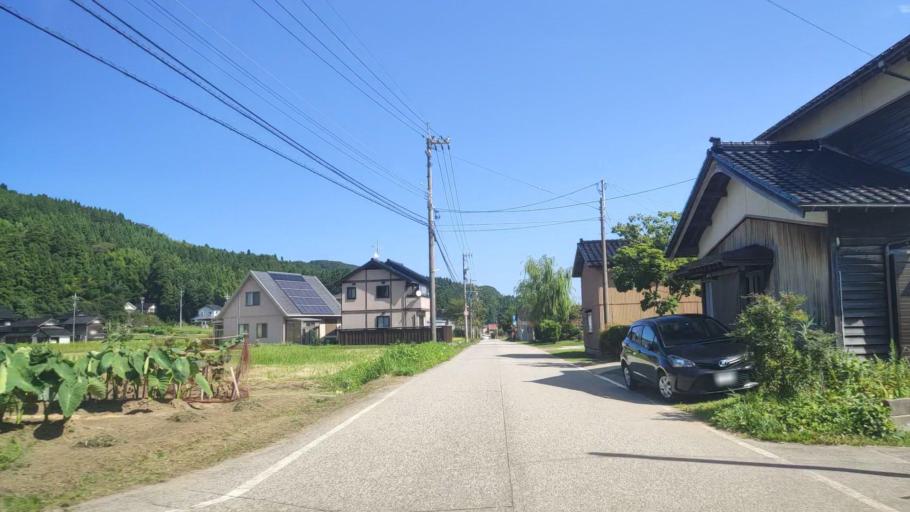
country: JP
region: Ishikawa
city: Nanao
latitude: 37.3780
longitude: 136.8789
